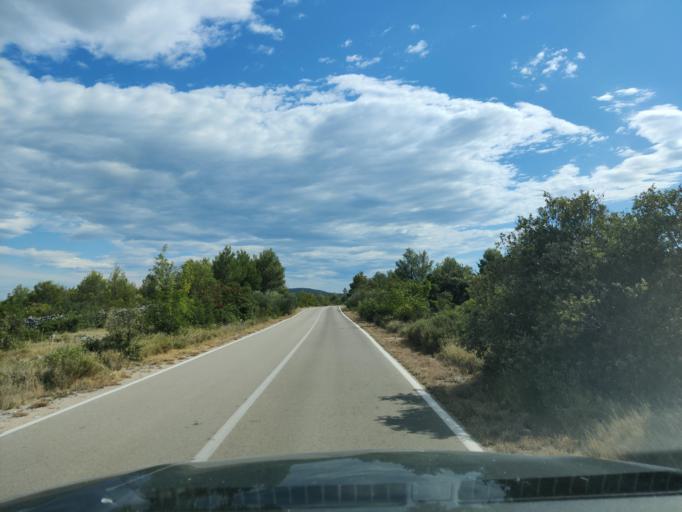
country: HR
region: Sibensko-Kniniska
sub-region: Grad Sibenik
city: Sibenik
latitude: 43.7360
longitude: 15.8578
